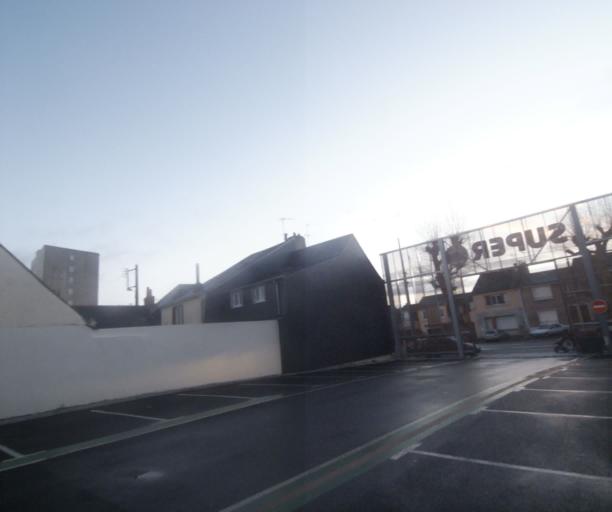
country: FR
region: Pays de la Loire
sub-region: Departement de la Sarthe
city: Le Mans
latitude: 48.0028
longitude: 0.1849
